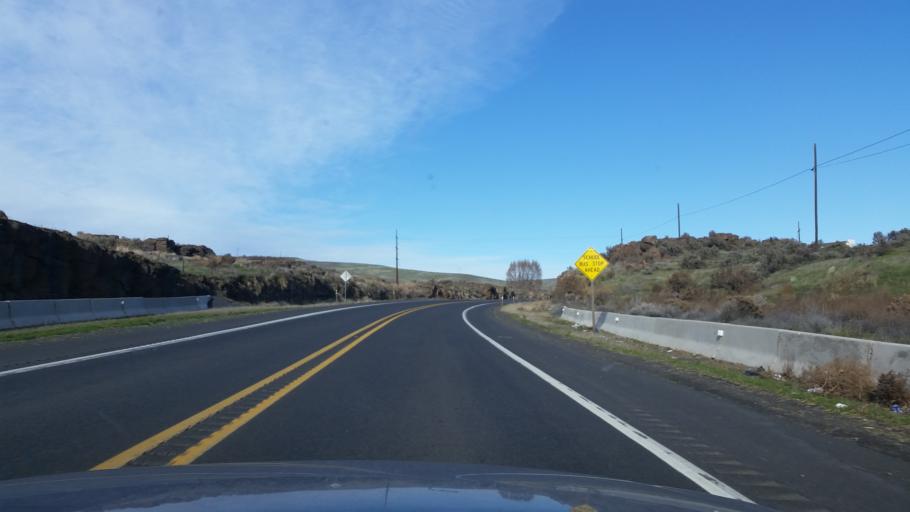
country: US
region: Washington
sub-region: Grant County
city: Ephrata
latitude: 47.2782
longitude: -119.5804
